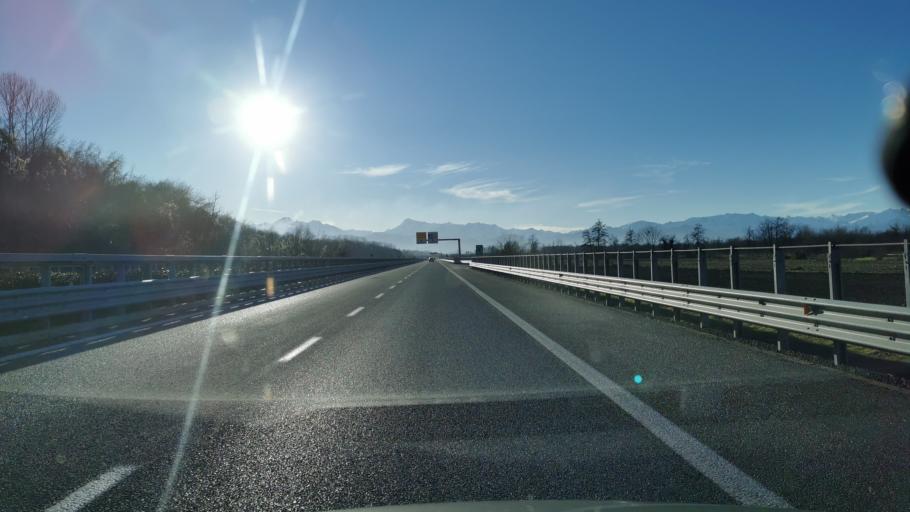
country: IT
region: Piedmont
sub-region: Provincia di Cuneo
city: Castelletto Stura
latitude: 44.4400
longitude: 7.6267
